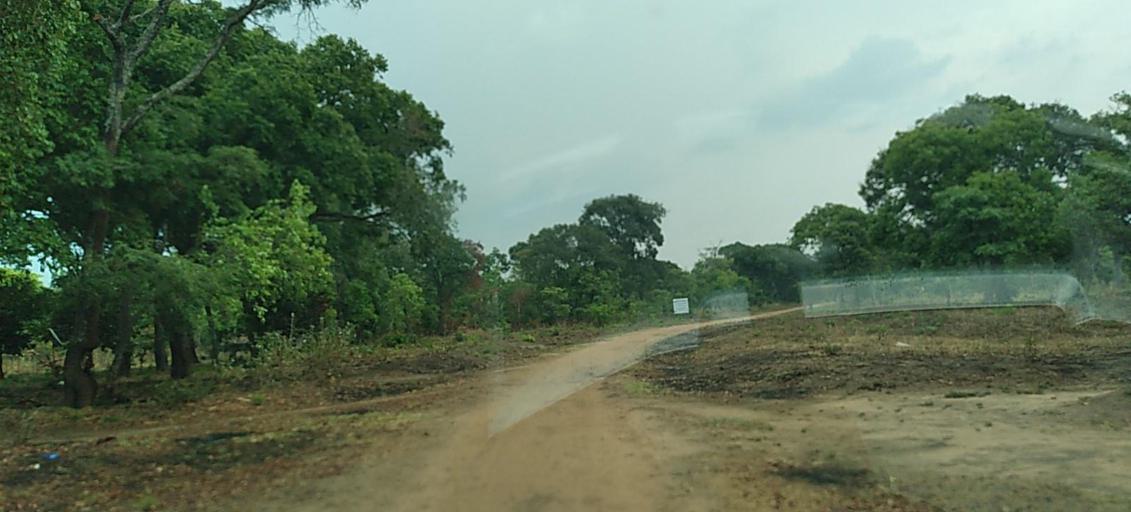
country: ZM
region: North-Western
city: Mwinilunga
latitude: -11.4526
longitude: 24.5889
